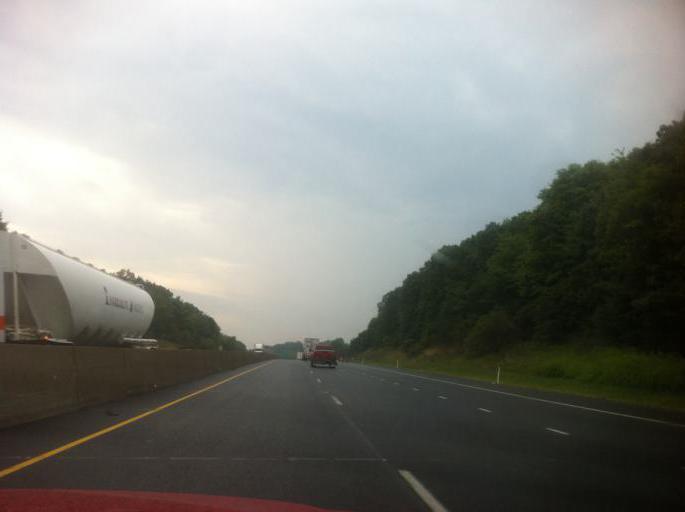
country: US
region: Pennsylvania
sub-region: Clarion County
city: Clarion
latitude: 41.1905
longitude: -79.4200
